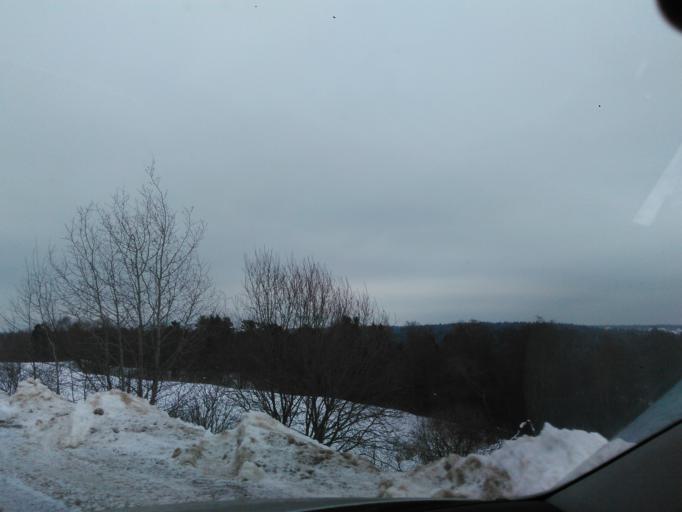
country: RU
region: Moskovskaya
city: Podosinki
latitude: 56.2760
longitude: 37.5971
